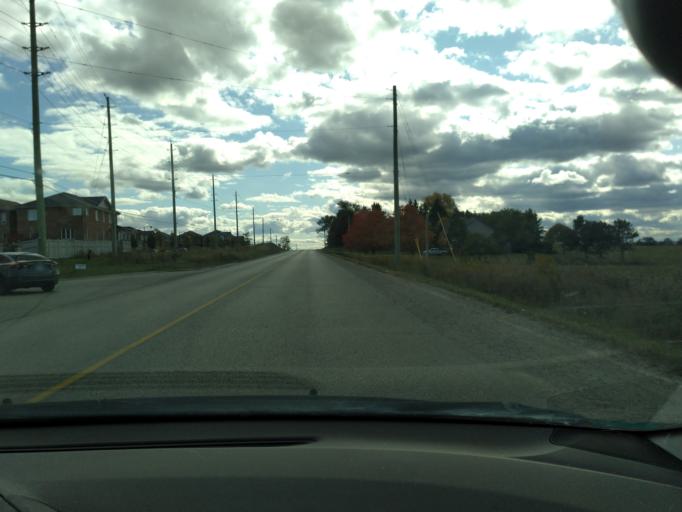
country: CA
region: Ontario
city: Bradford West Gwillimbury
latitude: 44.1027
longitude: -79.6009
